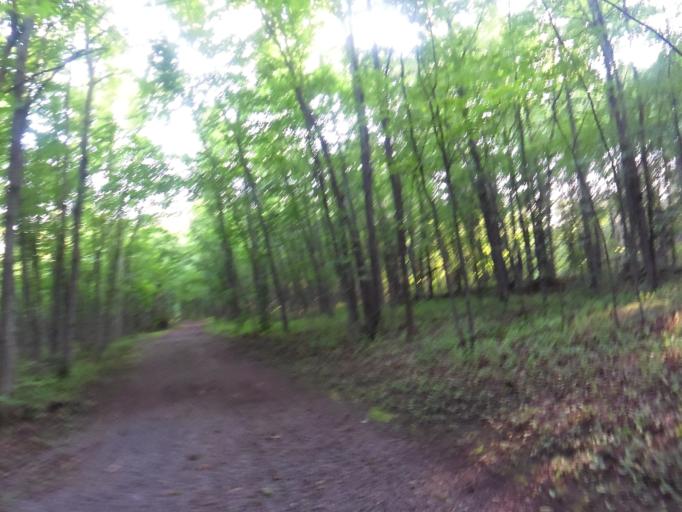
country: CA
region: Ontario
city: Bells Corners
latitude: 45.3101
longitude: -75.8164
